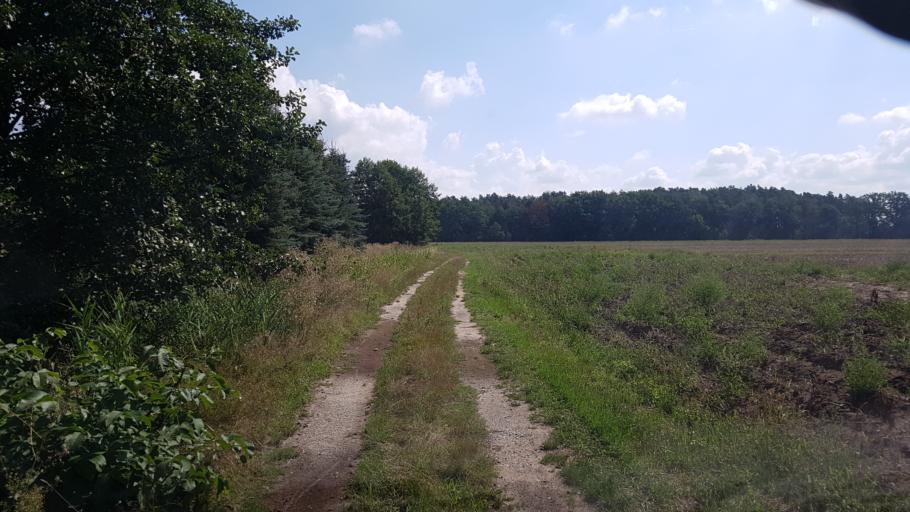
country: DE
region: Brandenburg
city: Sonnewalde
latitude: 51.6753
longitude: 13.6808
